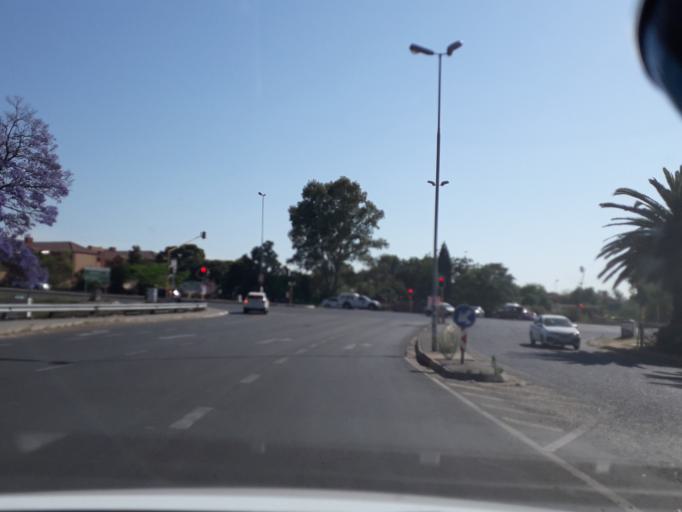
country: ZA
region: Gauteng
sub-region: City of Johannesburg Metropolitan Municipality
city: Roodepoort
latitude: -26.0869
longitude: 27.9343
